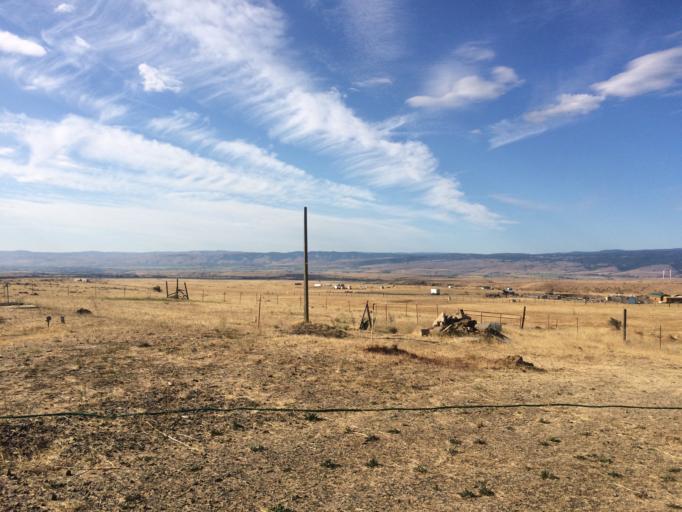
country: US
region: Washington
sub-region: Kittitas County
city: Ellensburg
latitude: 47.1558
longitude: -120.6326
